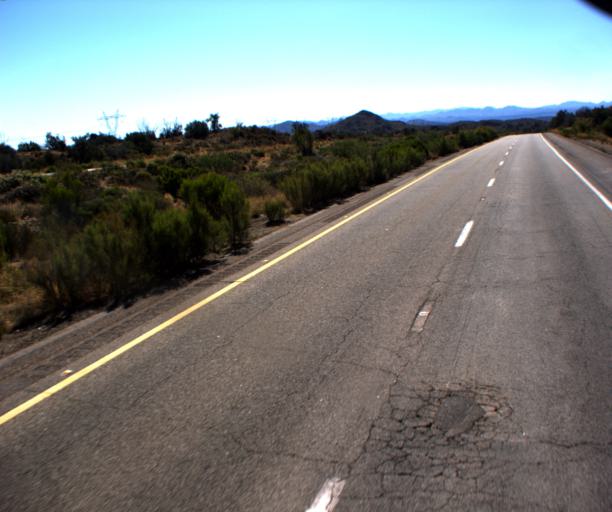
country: US
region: Arizona
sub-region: Yavapai County
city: Bagdad
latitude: 34.4718
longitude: -113.3183
